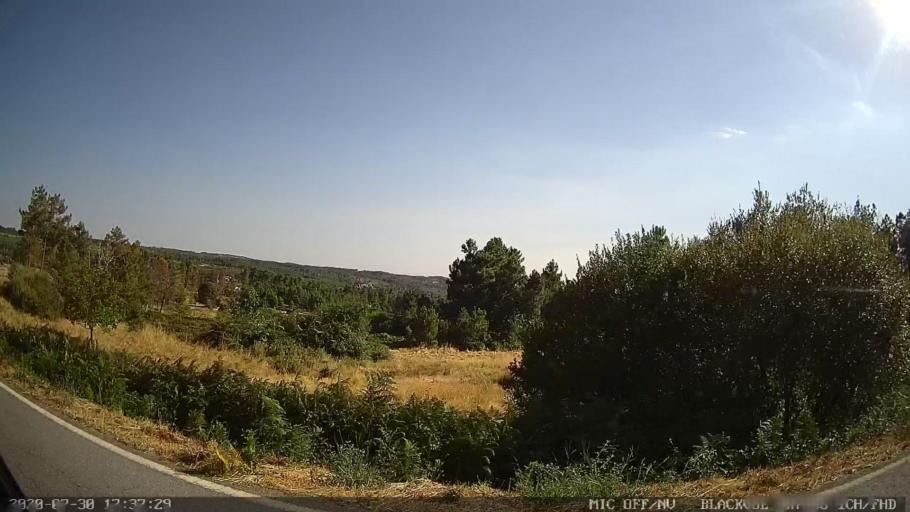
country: PT
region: Vila Real
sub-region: Murca
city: Murca
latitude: 41.3667
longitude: -7.4936
